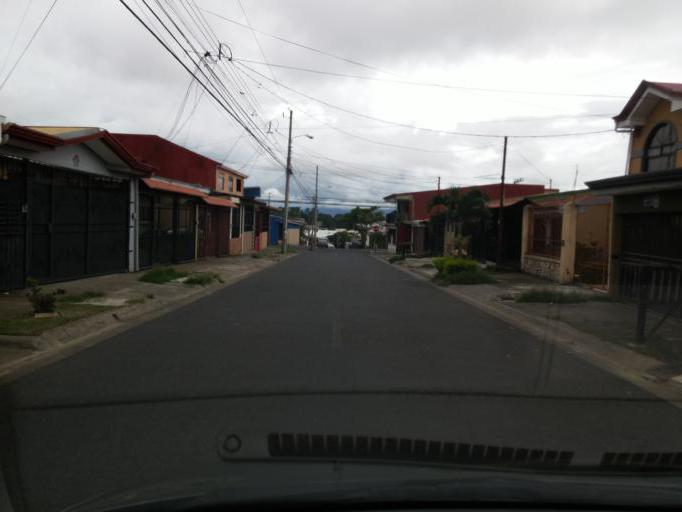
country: CR
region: Heredia
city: Mercedes
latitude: 10.0234
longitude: -84.1305
